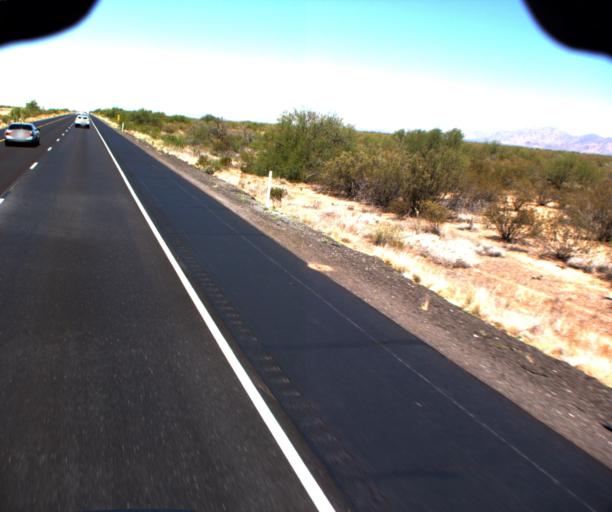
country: US
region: Arizona
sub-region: Yavapai County
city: Congress
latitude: 34.0824
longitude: -112.8915
